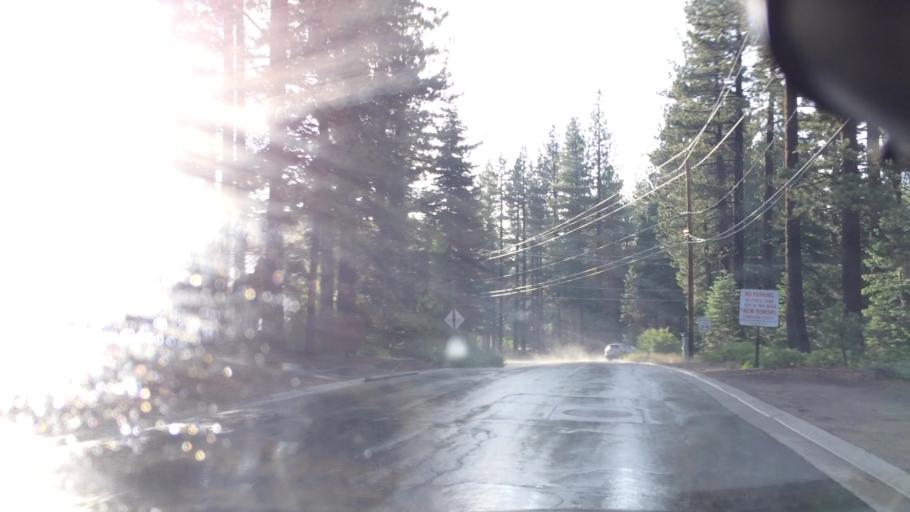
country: US
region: California
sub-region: El Dorado County
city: South Lake Tahoe
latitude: 38.8849
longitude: -119.9853
